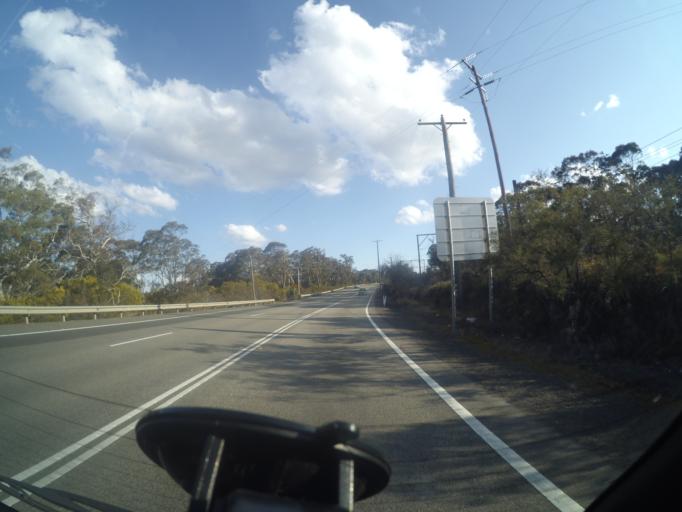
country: AU
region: New South Wales
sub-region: Blue Mountains Municipality
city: Blackheath
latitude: -33.6516
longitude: 150.2848
